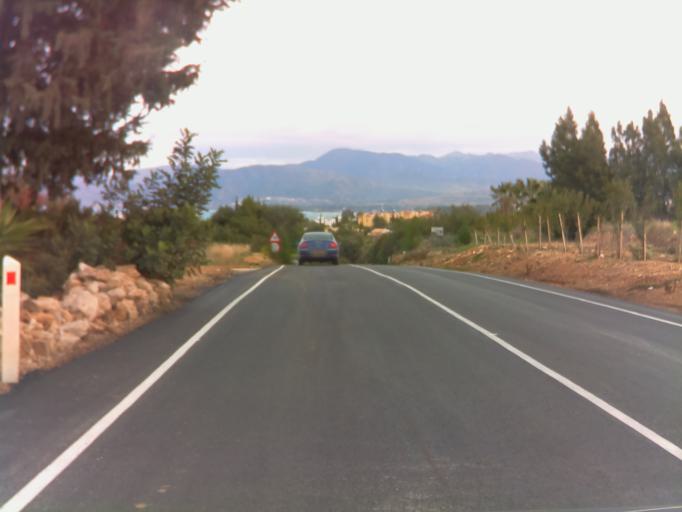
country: CY
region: Pafos
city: Polis
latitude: 35.0388
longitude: 32.3790
